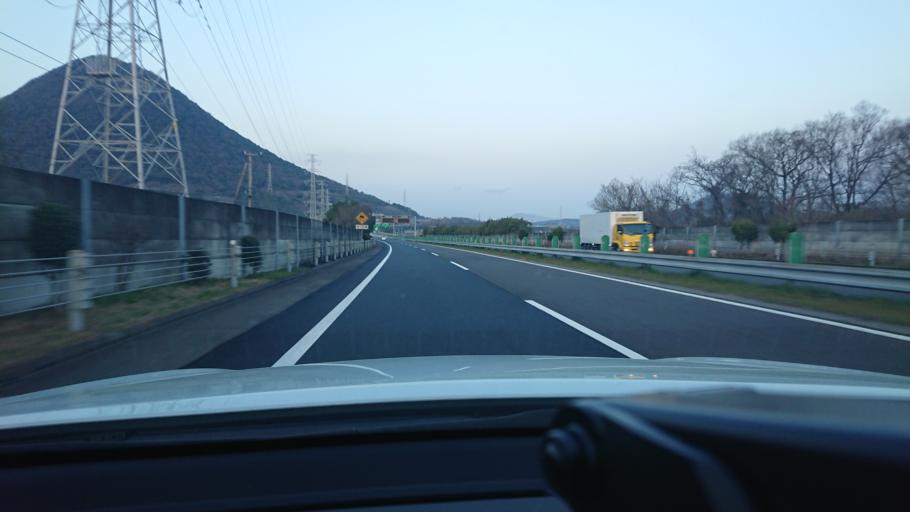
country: JP
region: Kagawa
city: Sakaidecho
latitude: 34.2812
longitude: 133.8643
